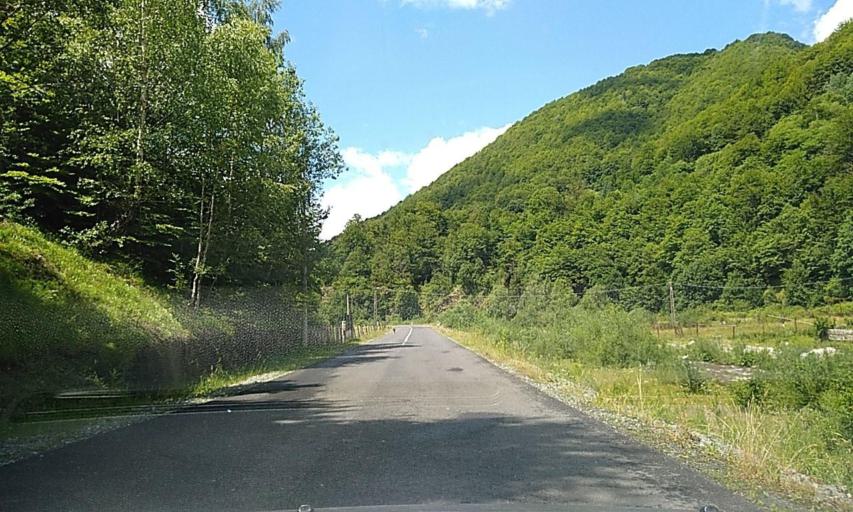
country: RO
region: Hunedoara
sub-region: Oras Petrila
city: Petrila
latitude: 45.4177
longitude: 23.4570
